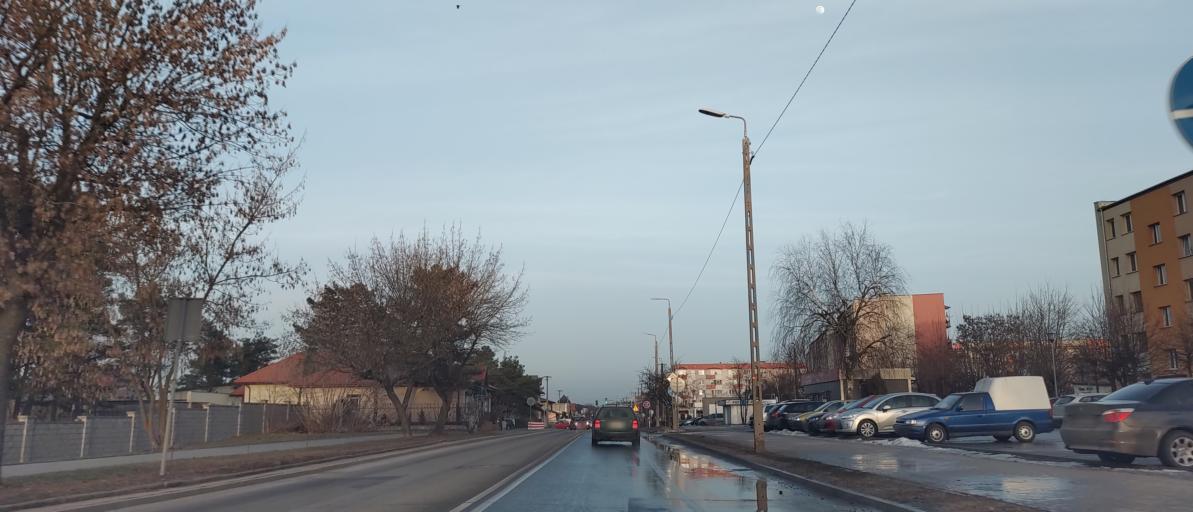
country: PL
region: Masovian Voivodeship
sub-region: Powiat bialobrzeski
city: Bialobrzegi
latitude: 51.6439
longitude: 20.9474
